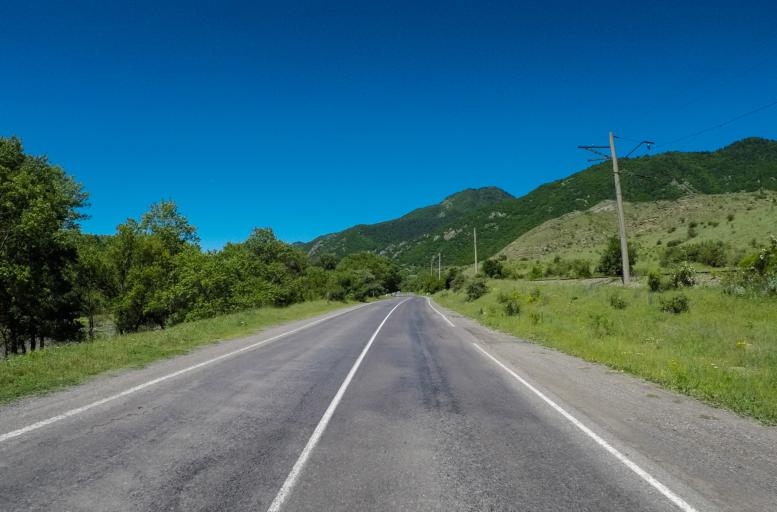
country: GE
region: Samtskhe-Javakheti
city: Aspindza
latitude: 41.7442
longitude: 43.1969
